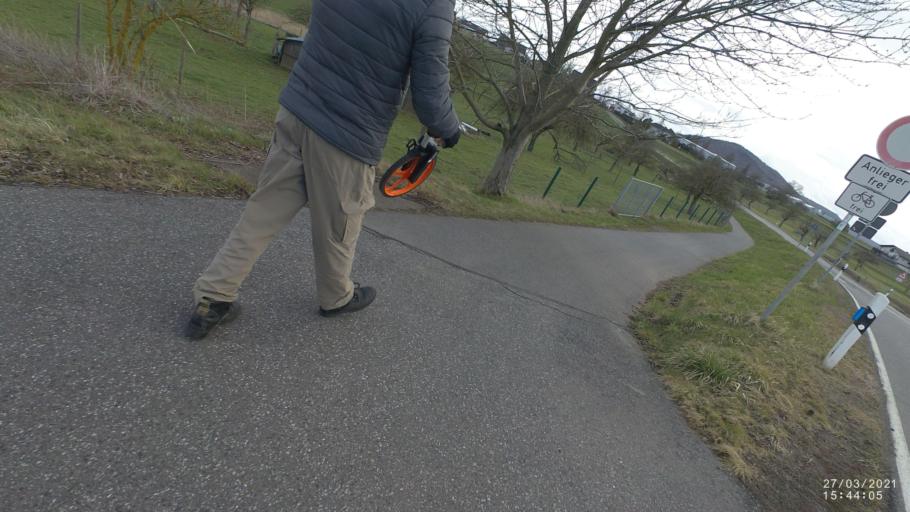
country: DE
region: Rheinland-Pfalz
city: Bell
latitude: 50.3934
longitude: 7.2342
